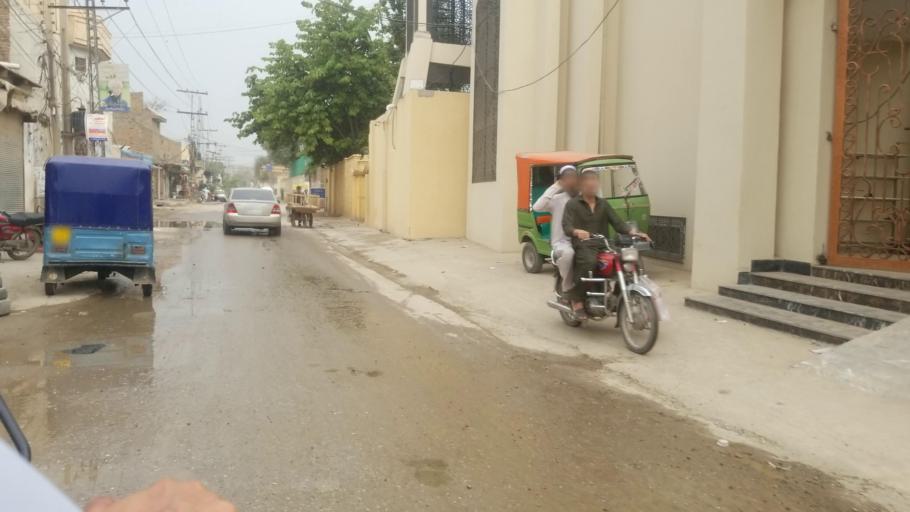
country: PK
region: Khyber Pakhtunkhwa
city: Peshawar
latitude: 33.9859
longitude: 71.5538
